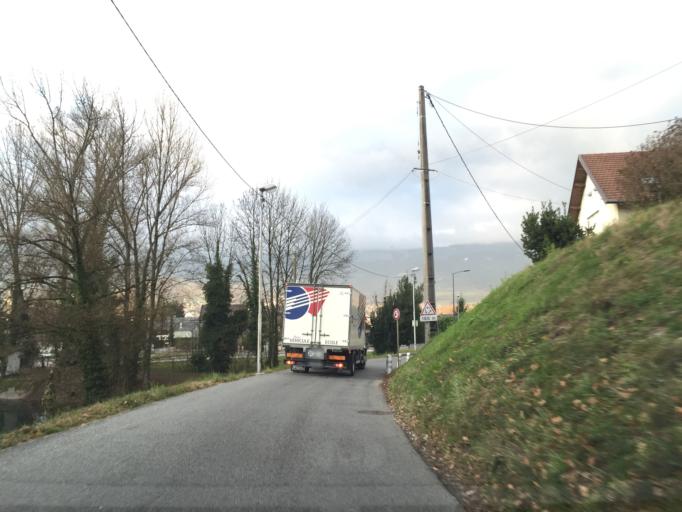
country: FR
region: Rhone-Alpes
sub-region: Departement de la Savoie
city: Sonnaz
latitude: 45.5978
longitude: 5.9069
